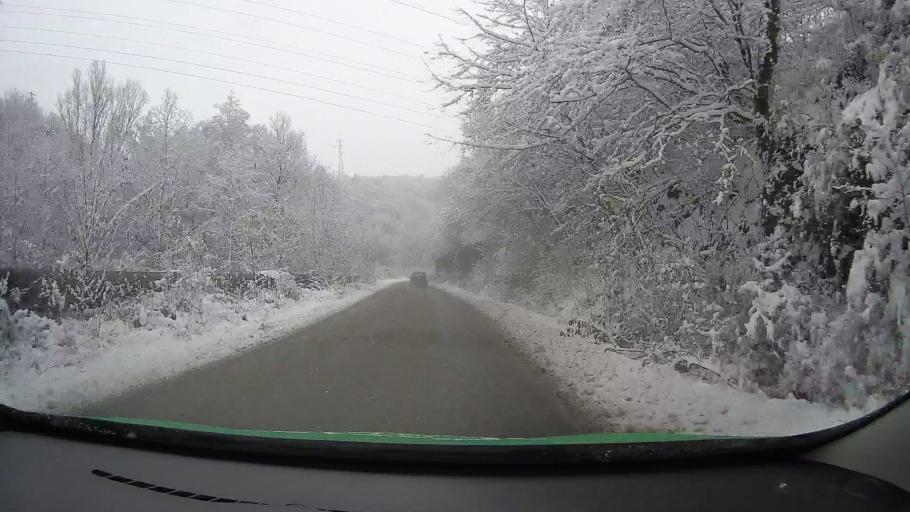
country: RO
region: Hunedoara
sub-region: Comuna Teliucu Inferior
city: Teliucu Inferior
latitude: 45.7310
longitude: 22.8813
